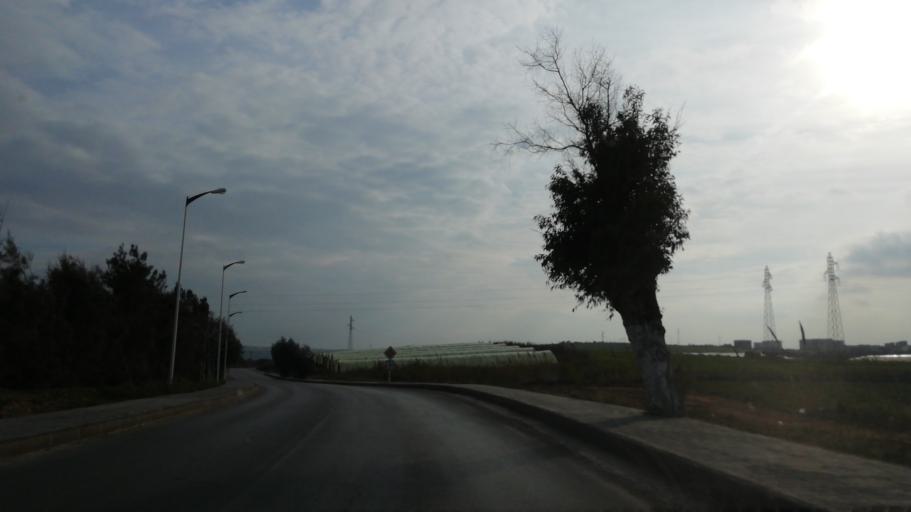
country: DZ
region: Mostaganem
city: Mostaganem
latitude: 35.8899
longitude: 0.0760
